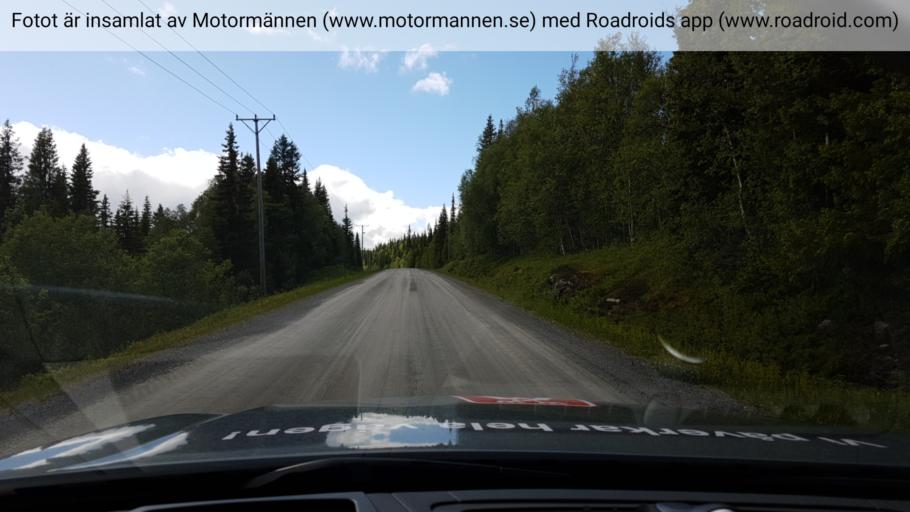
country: SE
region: Jaemtland
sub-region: Are Kommun
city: Are
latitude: 63.6728
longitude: 12.8443
